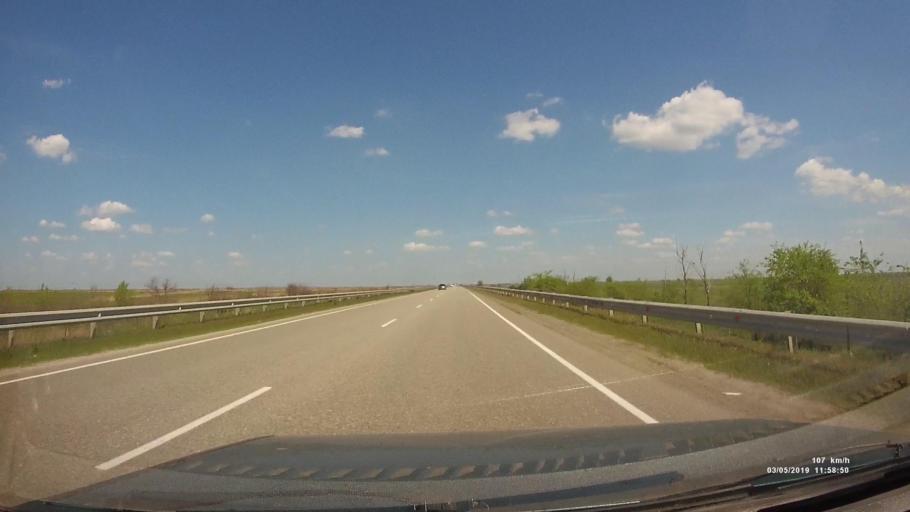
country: RU
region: Rostov
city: Bagayevskaya
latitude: 47.2263
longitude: 40.3241
